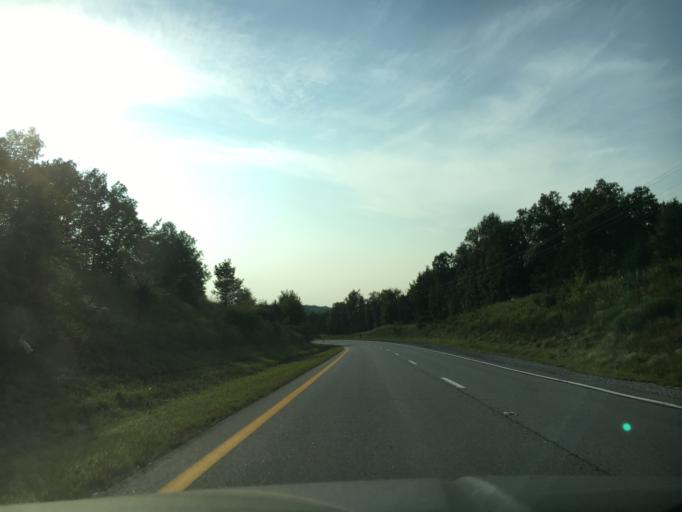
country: US
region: Virginia
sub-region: Prince Edward County
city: Farmville
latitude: 37.2744
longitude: -78.3111
